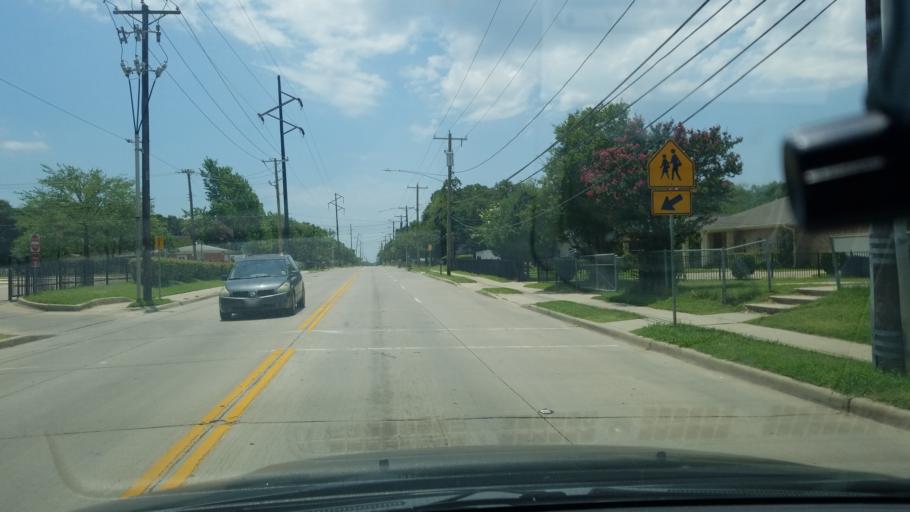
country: US
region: Texas
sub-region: Dallas County
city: Balch Springs
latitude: 32.7307
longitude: -96.6569
